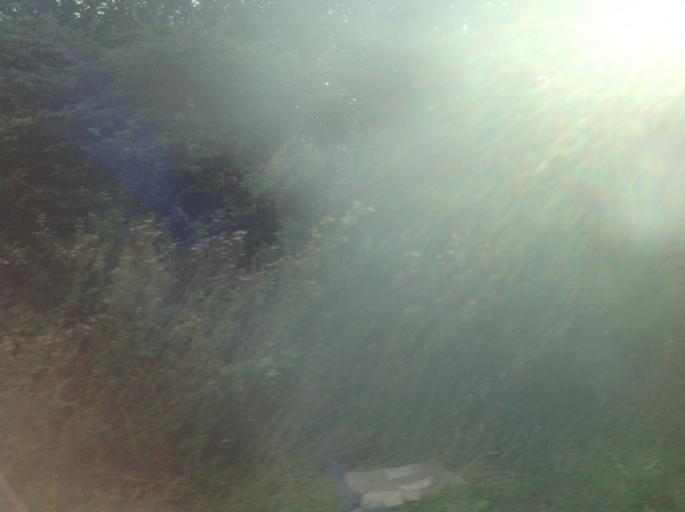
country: GB
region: England
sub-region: Suffolk
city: Felixstowe
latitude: 51.9952
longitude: 1.3117
